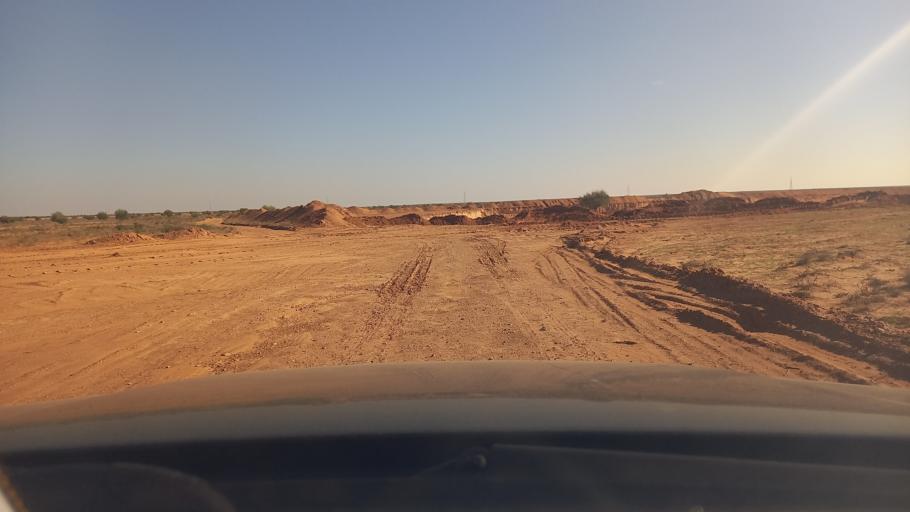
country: TN
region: Madanin
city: Medenine
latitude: 33.1732
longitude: 10.5309
